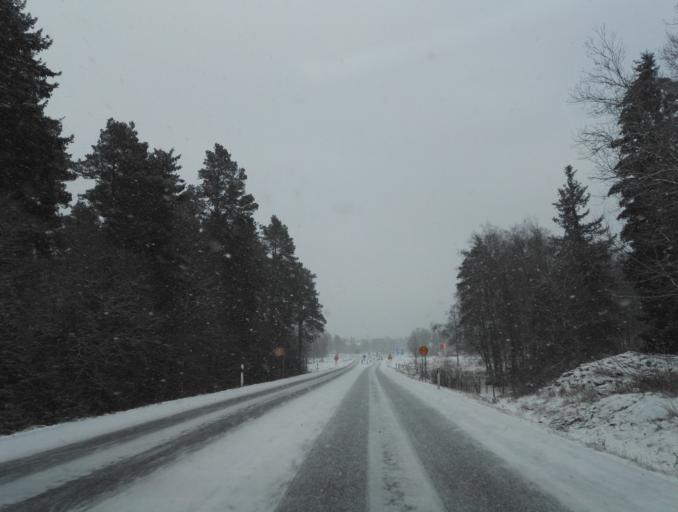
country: SE
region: Kronoberg
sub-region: Uppvidinge Kommun
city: Lenhovda
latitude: 56.9993
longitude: 15.2776
